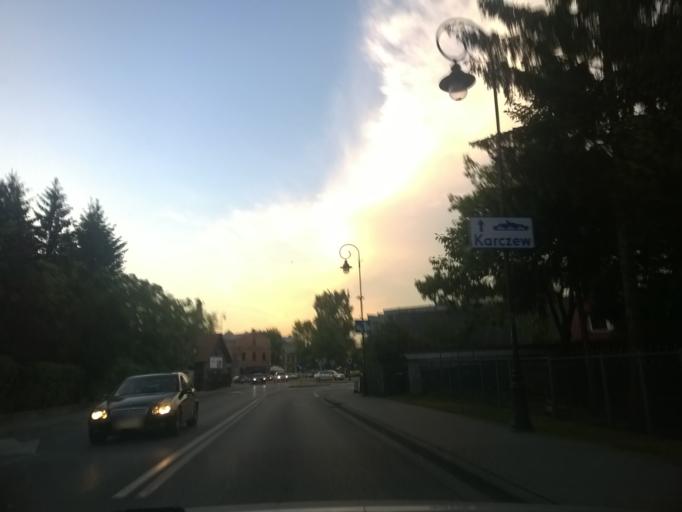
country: PL
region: Masovian Voivodeship
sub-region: Powiat piaseczynski
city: Konstancin-Jeziorna
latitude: 52.0896
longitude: 21.1217
